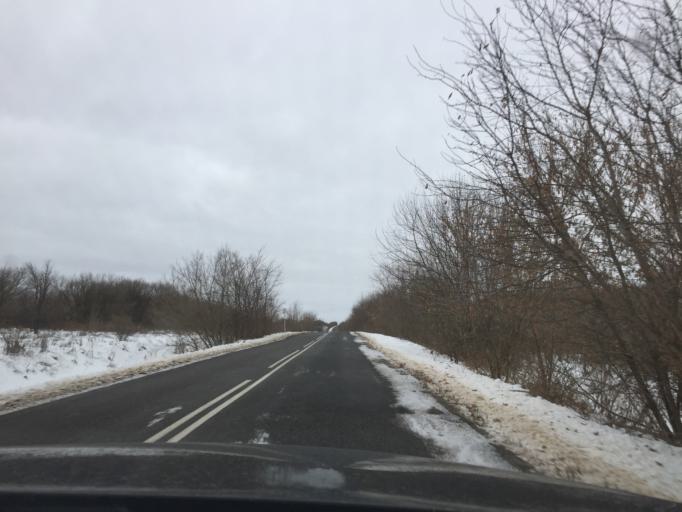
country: RU
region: Tula
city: Teploye
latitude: 53.7916
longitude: 37.6078
